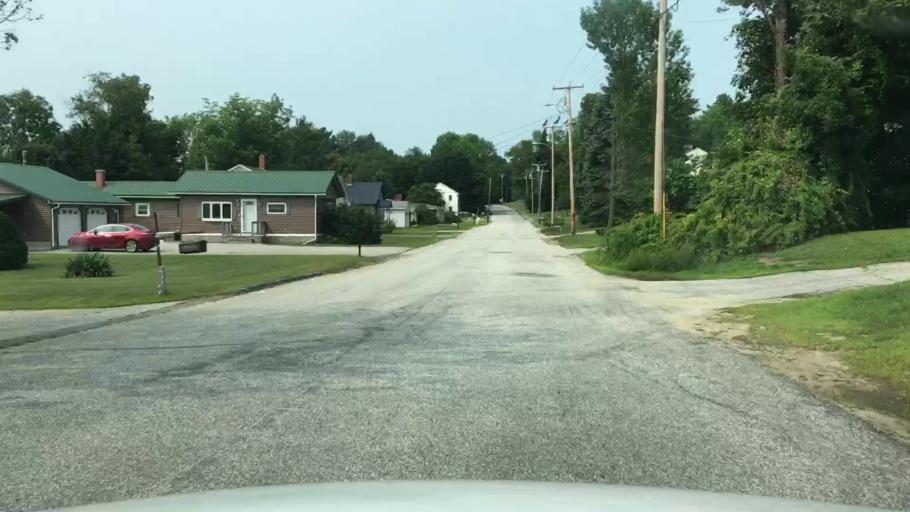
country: US
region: Maine
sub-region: Androscoggin County
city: Livermore Falls
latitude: 44.4812
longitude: -70.1870
